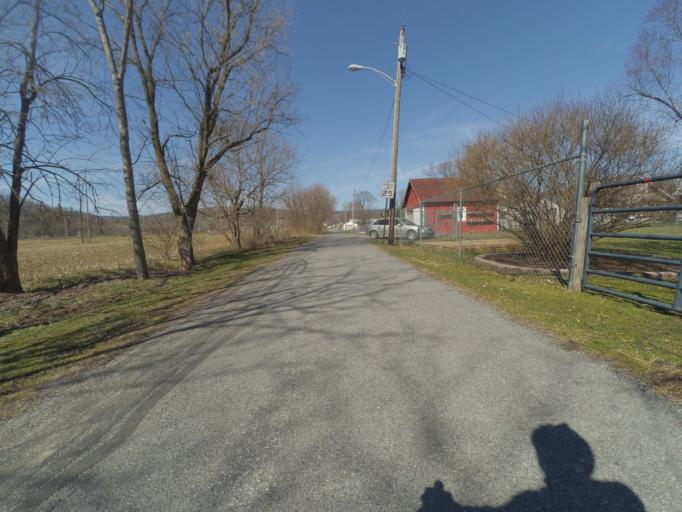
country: US
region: Pennsylvania
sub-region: Centre County
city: Milesburg
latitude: 40.9379
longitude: -77.7862
